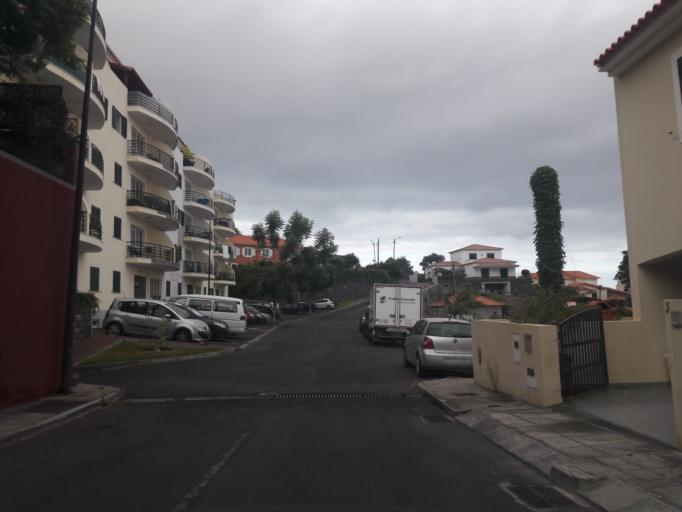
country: PT
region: Madeira
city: Canico
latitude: 32.6465
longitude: -16.8525
